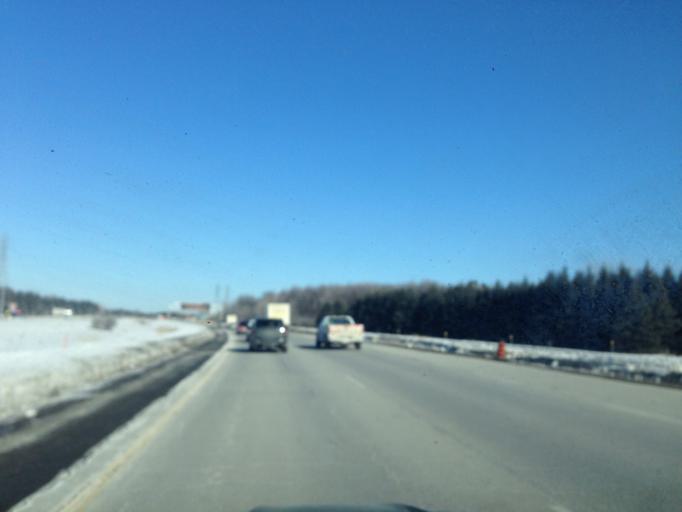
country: CA
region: Ontario
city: Ottawa
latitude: 45.4007
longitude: -75.5934
